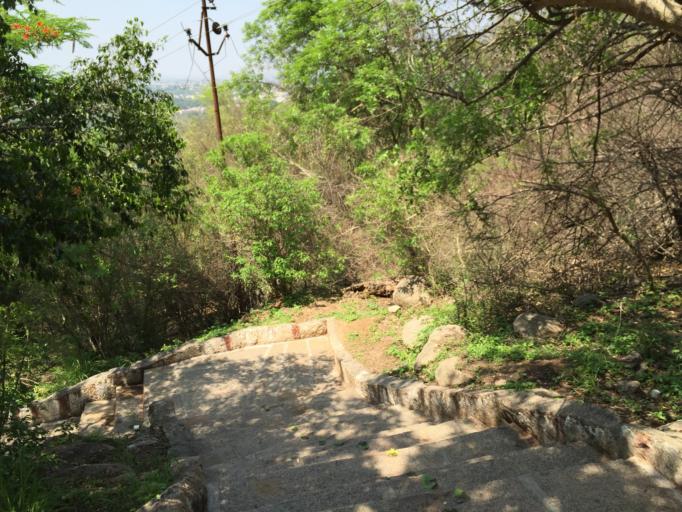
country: IN
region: Karnataka
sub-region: Mysore
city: Mysore
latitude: 12.2816
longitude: 76.6680
